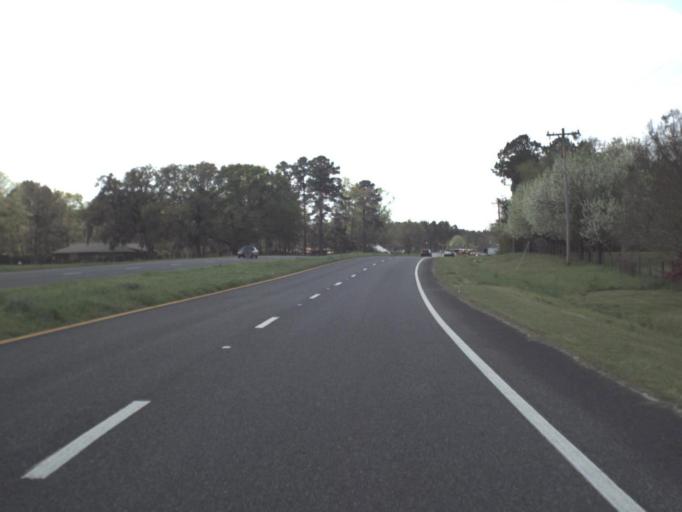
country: US
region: Florida
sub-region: Gadsden County
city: Havana
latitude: 30.6789
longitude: -84.3847
